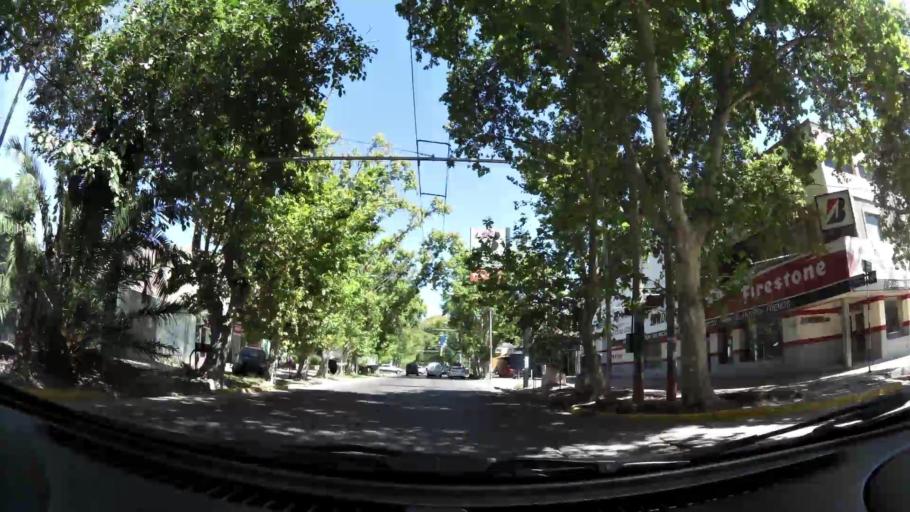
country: AR
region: Mendoza
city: Mendoza
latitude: -32.8943
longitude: -68.8222
